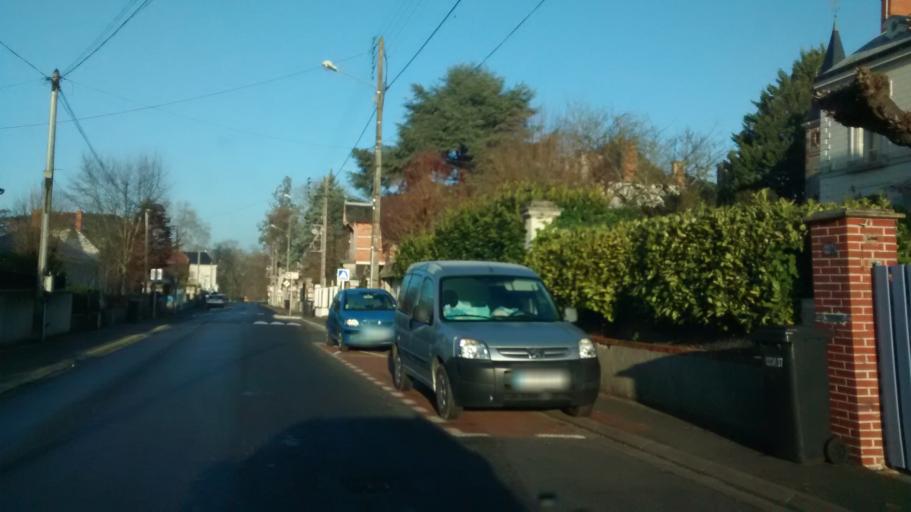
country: FR
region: Centre
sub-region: Departement d'Indre-et-Loire
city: Veigne
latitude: 47.2888
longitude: 0.7202
